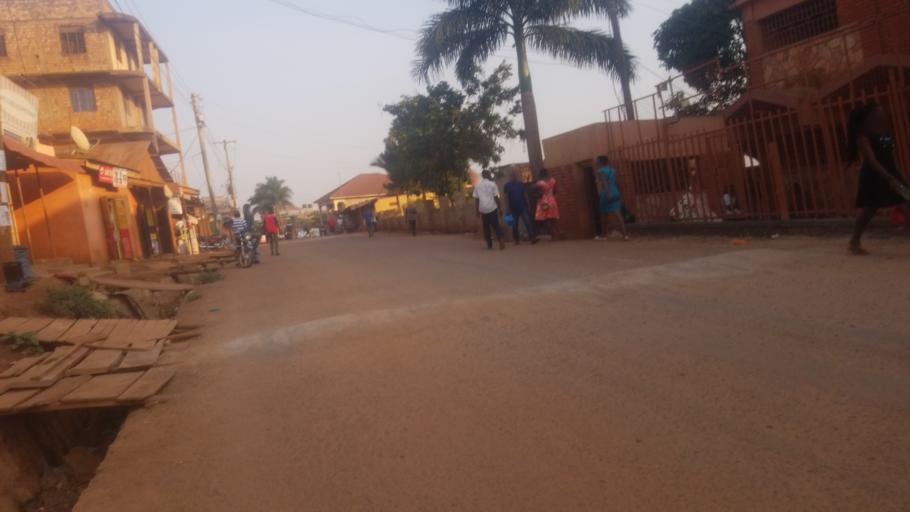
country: UG
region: Central Region
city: Kampala Central Division
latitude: 0.3365
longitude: 32.5616
